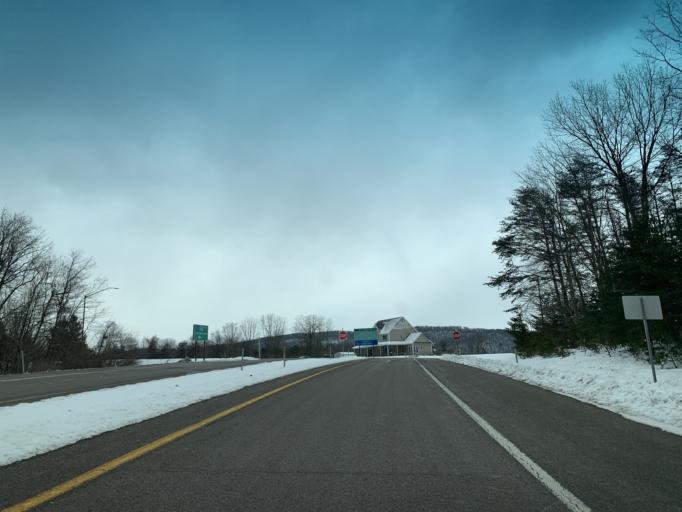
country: US
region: West Virginia
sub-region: Morgan County
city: Berkeley Springs
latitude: 39.6693
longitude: -78.4426
